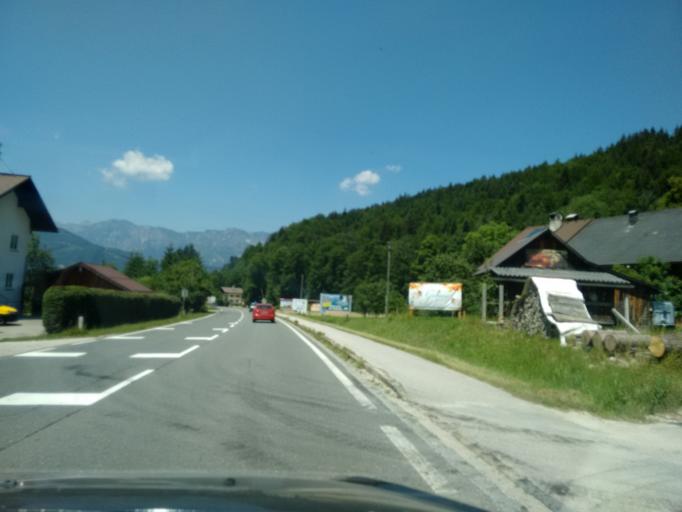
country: AT
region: Upper Austria
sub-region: Politischer Bezirk Gmunden
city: Bad Goisern
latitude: 47.6253
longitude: 13.6435
